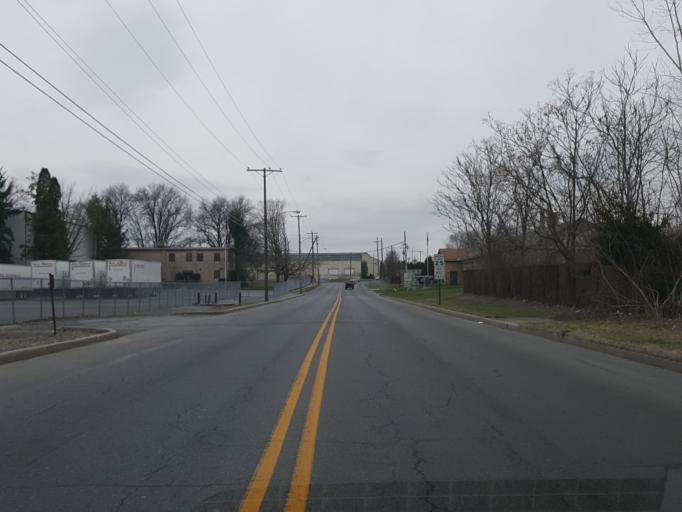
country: US
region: Pennsylvania
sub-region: Lebanon County
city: Pleasant Hill
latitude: 40.3447
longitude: -76.4384
